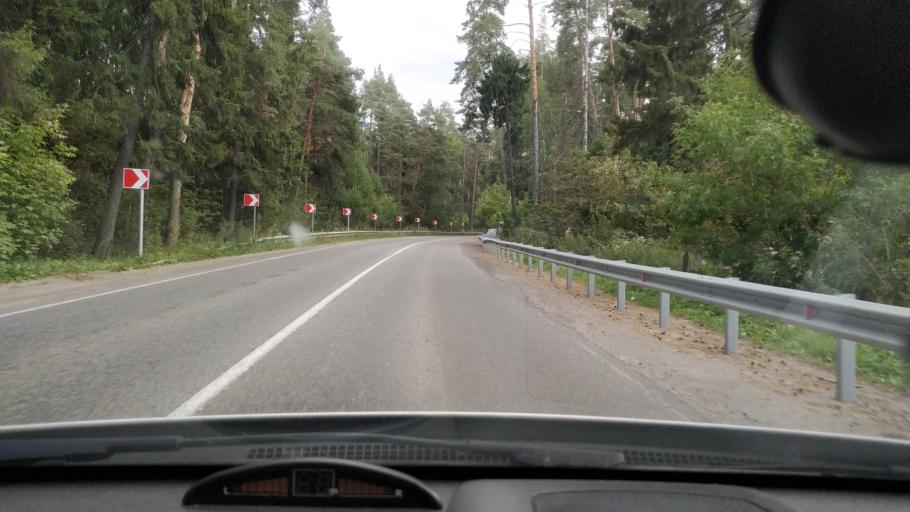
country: RU
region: Moskovskaya
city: Zheleznodorozhnyy
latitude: 55.7998
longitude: 38.0266
